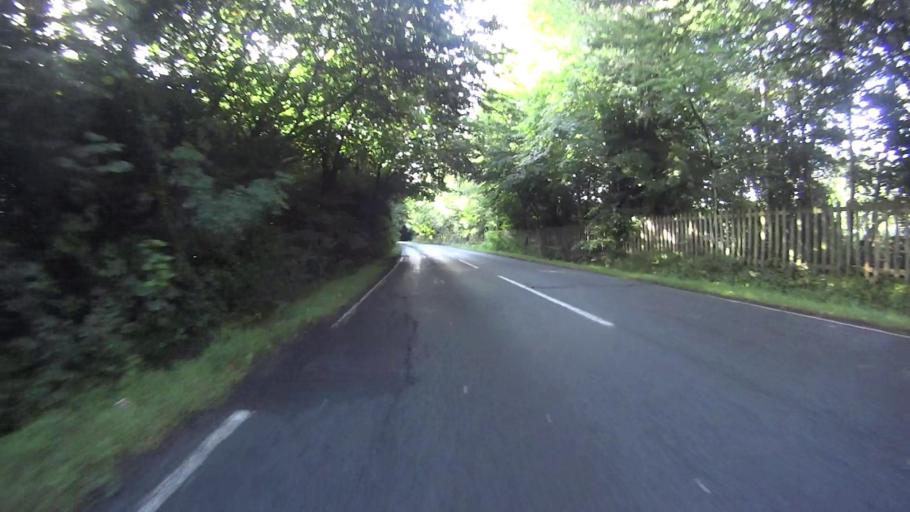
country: GB
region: England
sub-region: Surrey
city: Felbridge
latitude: 51.1484
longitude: -0.0226
